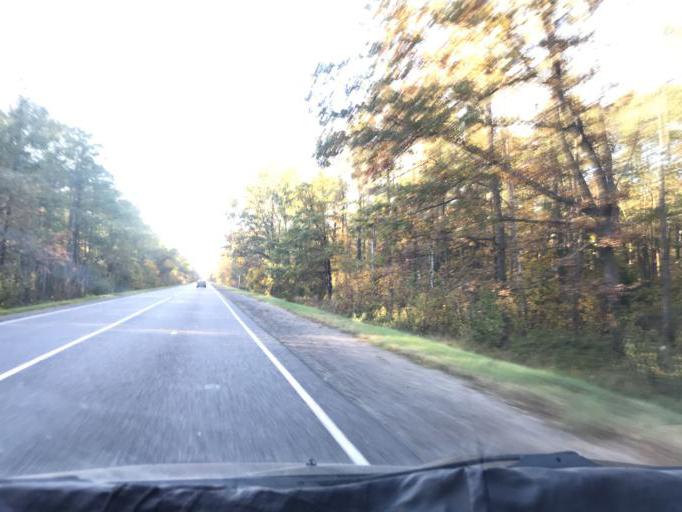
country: BY
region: Gomel
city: Pyetrykaw
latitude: 52.2605
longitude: 28.3284
